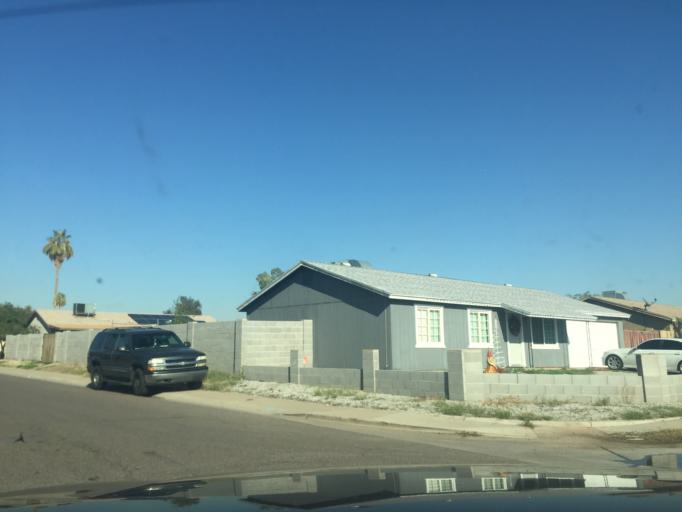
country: US
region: Arizona
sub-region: Maricopa County
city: Tolleson
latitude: 33.4691
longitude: -112.2146
